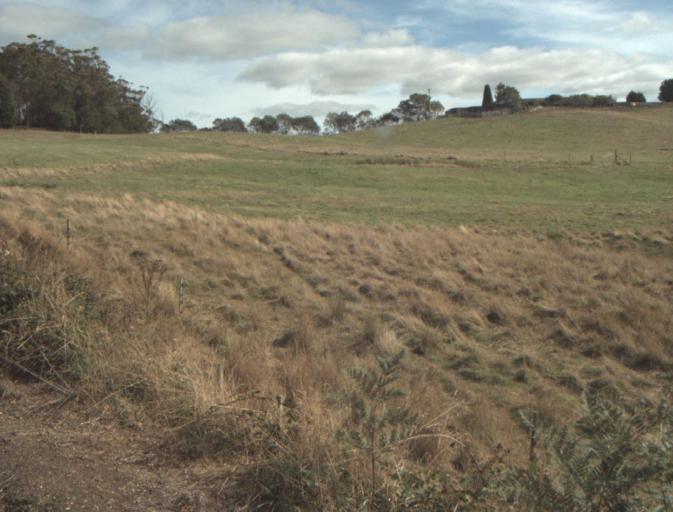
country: AU
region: Tasmania
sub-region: Launceston
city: Mayfield
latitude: -41.1817
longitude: 147.1942
